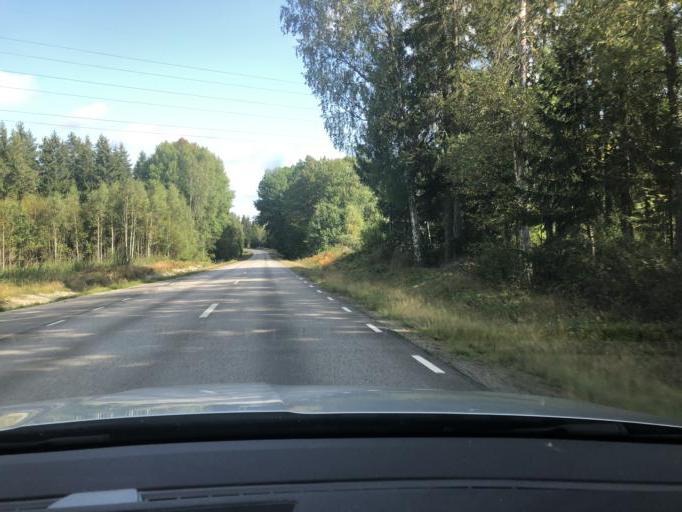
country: SE
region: Blekinge
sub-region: Karlshamns Kommun
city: Svangsta
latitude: 56.4273
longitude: 14.6677
